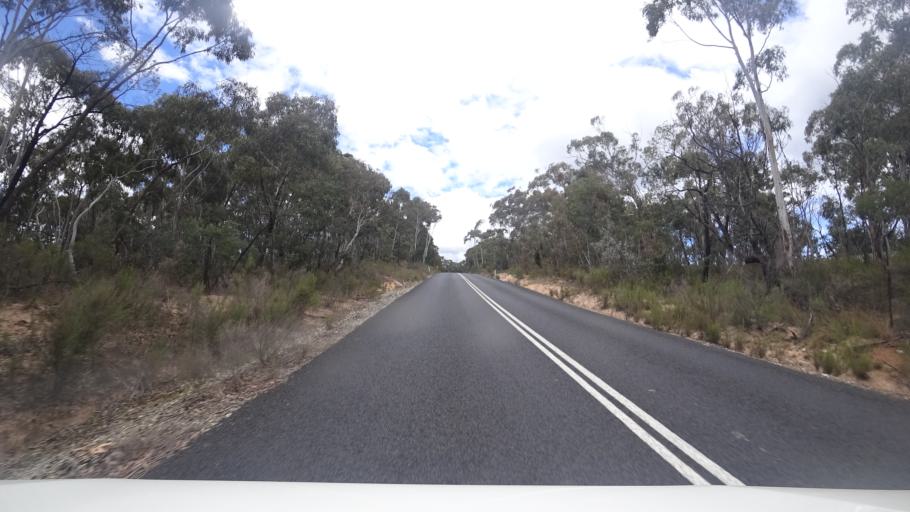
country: AU
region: New South Wales
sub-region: Oberon
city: Oberon
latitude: -33.6242
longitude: 149.8909
